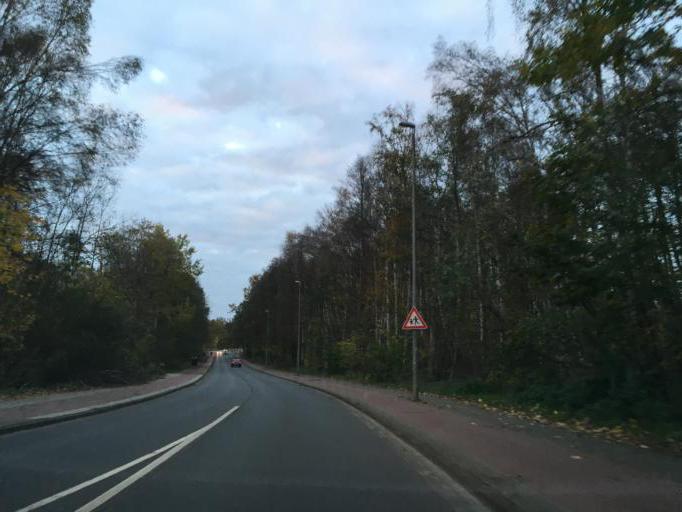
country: DE
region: Lower Saxony
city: Lueneburg
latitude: 53.2414
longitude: 10.4346
